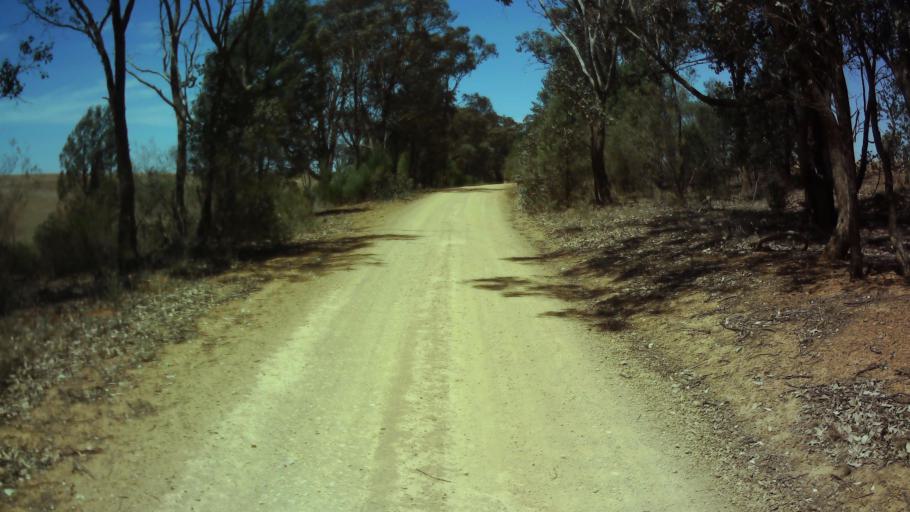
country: AU
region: New South Wales
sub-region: Weddin
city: Grenfell
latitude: -33.9283
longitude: 148.1724
